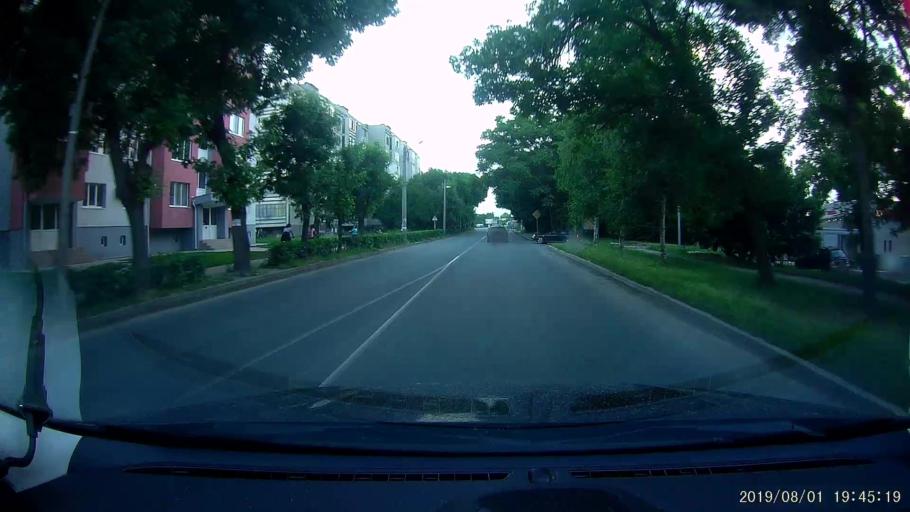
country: BG
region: Burgas
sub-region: Obshtina Karnobat
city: Karnobat
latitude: 42.6512
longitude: 26.9839
